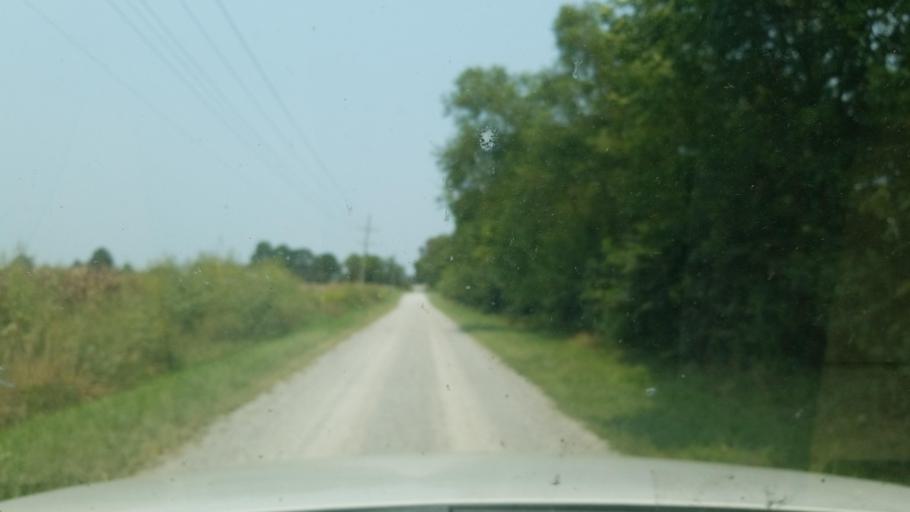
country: US
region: Illinois
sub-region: Saline County
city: Harrisburg
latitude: 37.8112
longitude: -88.5167
